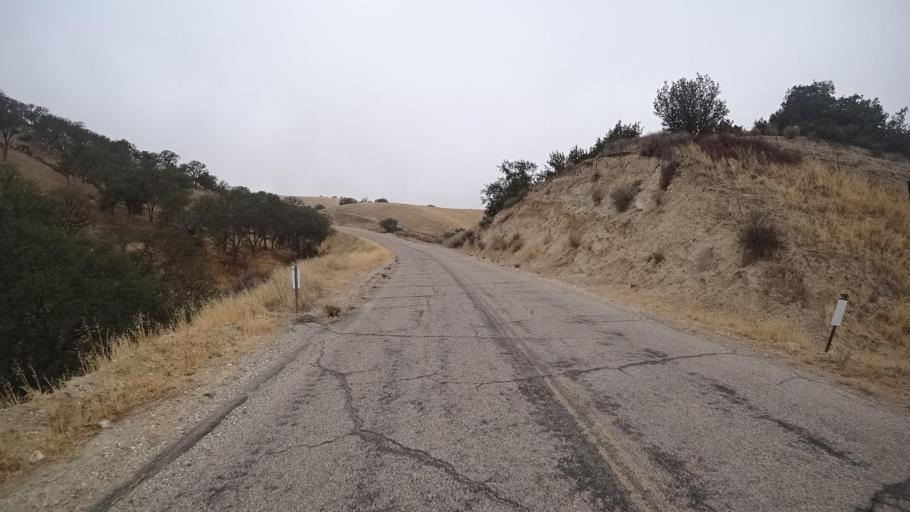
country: US
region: California
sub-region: San Luis Obispo County
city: San Miguel
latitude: 35.9118
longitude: -120.7107
